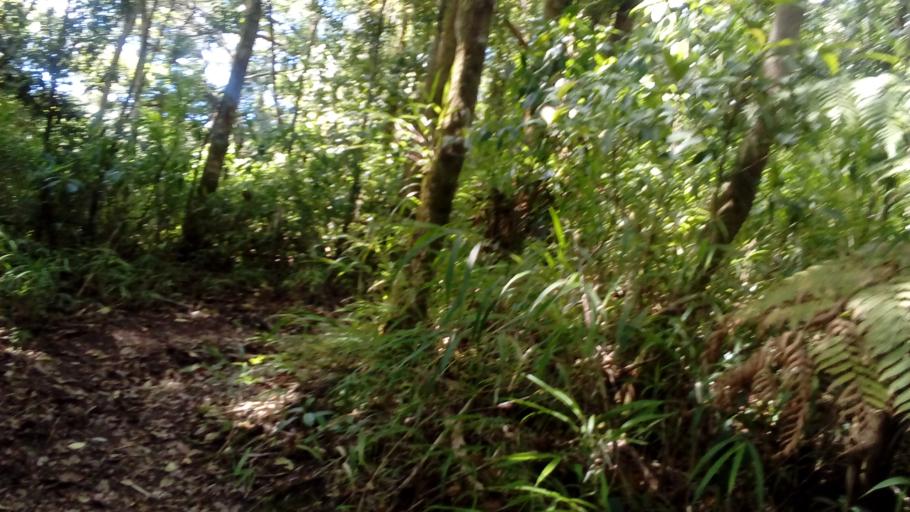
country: CR
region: Alajuela
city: Rio Segundo
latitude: 10.1621
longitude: -84.2363
